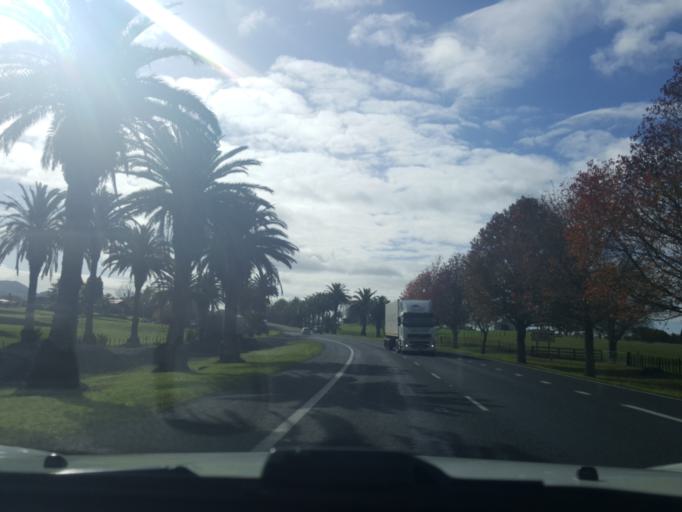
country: NZ
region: Waikato
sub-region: Hauraki District
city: Waihi
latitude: -37.4002
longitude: 175.8235
